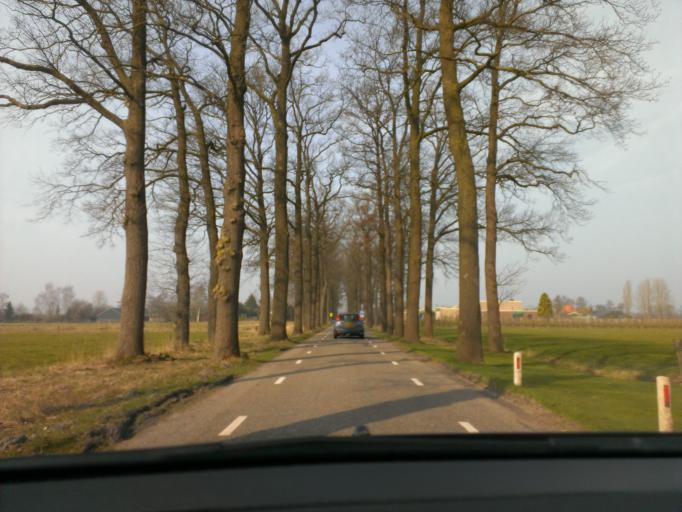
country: NL
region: Gelderland
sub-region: Gemeente Voorst
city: Twello
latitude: 52.2504
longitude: 6.0409
